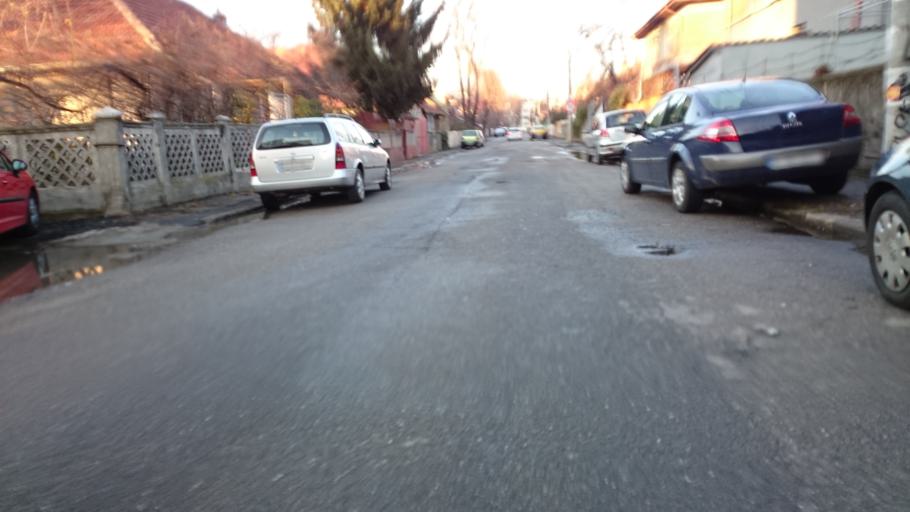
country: RO
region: Bucuresti
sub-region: Municipiul Bucuresti
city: Bucuresti
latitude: 44.4242
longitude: 26.0586
